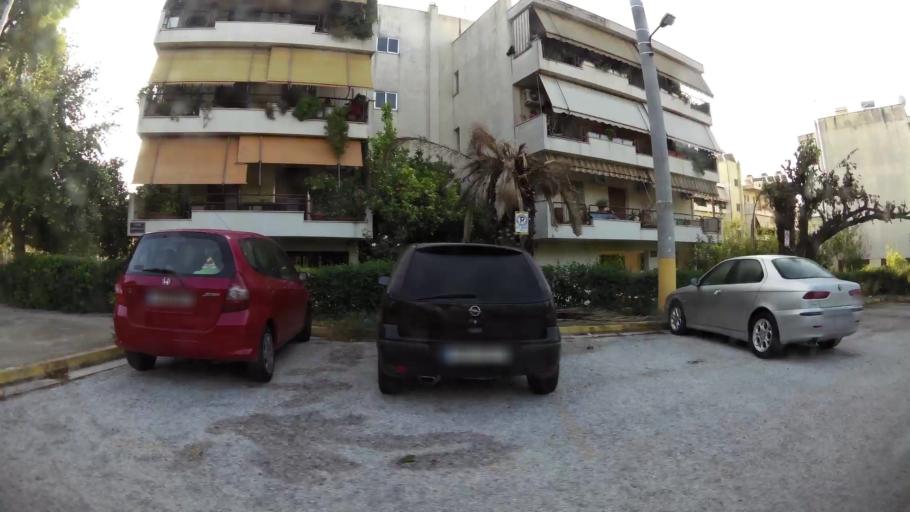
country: GR
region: Attica
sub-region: Nomarchia Athinas
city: Agioi Anargyroi
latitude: 38.0464
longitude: 23.7246
